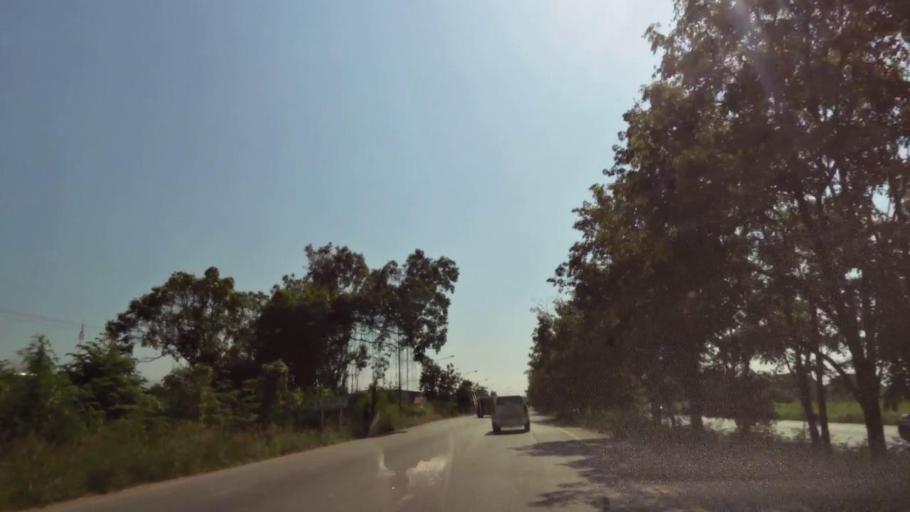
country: TH
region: Nakhon Sawan
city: Kao Liao
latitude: 15.8722
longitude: 100.1164
